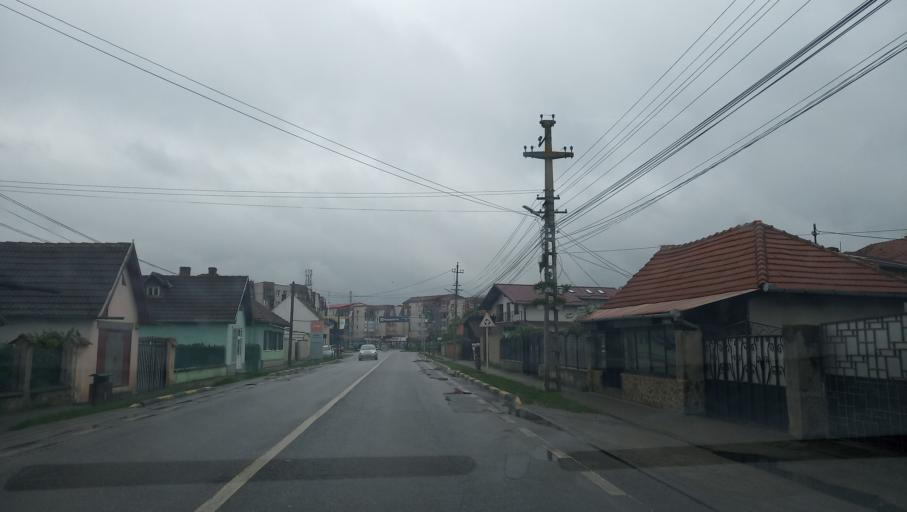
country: RO
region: Alba
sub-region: Municipiul Sebes
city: Sebes
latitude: 45.9541
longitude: 23.5793
